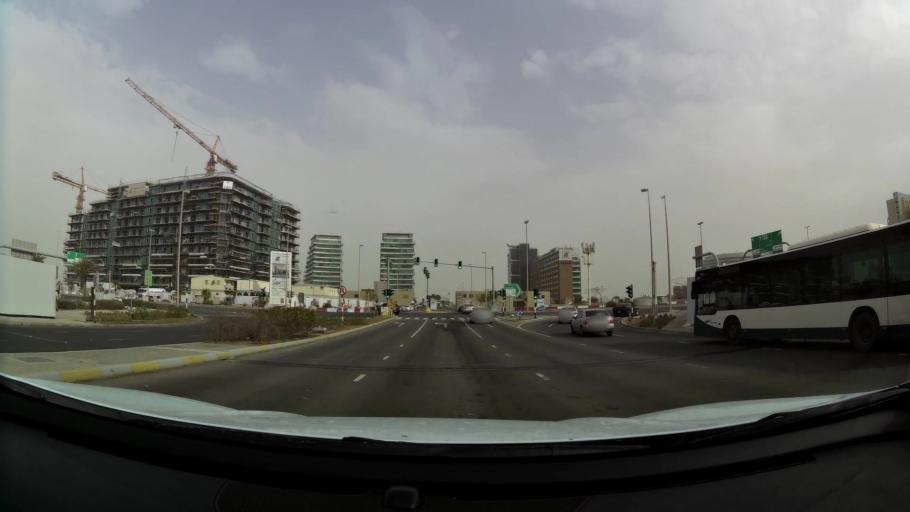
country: AE
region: Abu Dhabi
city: Abu Dhabi
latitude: 24.4477
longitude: 54.6006
